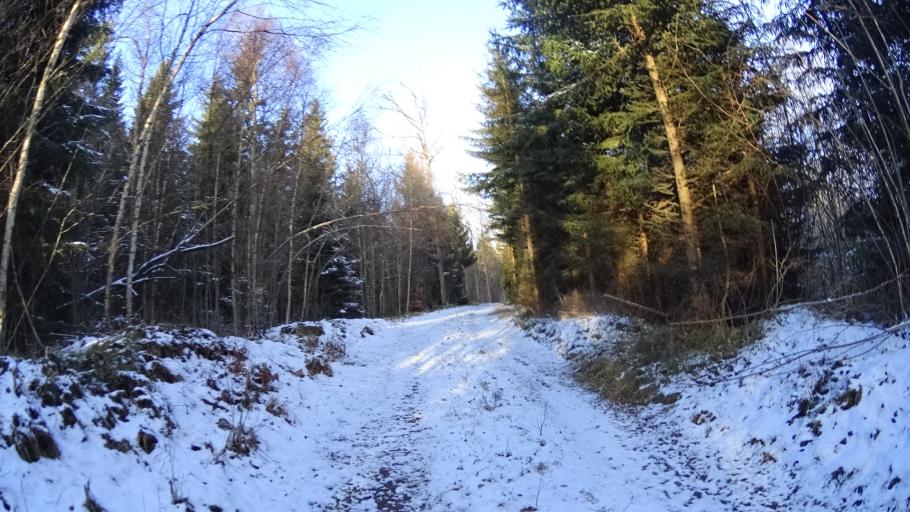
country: SE
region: Skane
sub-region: Hoors Kommun
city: Hoeoer
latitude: 55.9938
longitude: 13.5557
